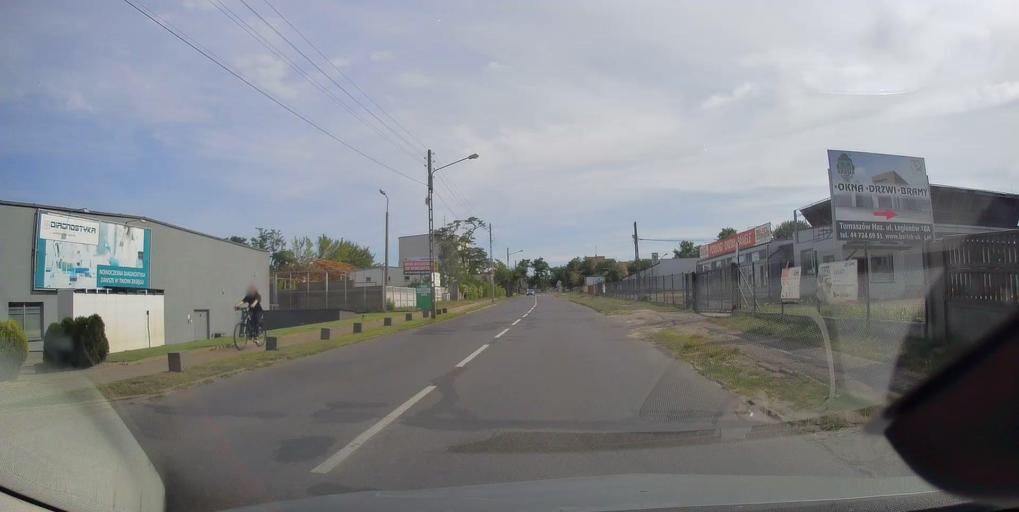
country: PL
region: Lodz Voivodeship
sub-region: Powiat tomaszowski
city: Tomaszow Mazowiecki
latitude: 51.5338
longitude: 19.9963
